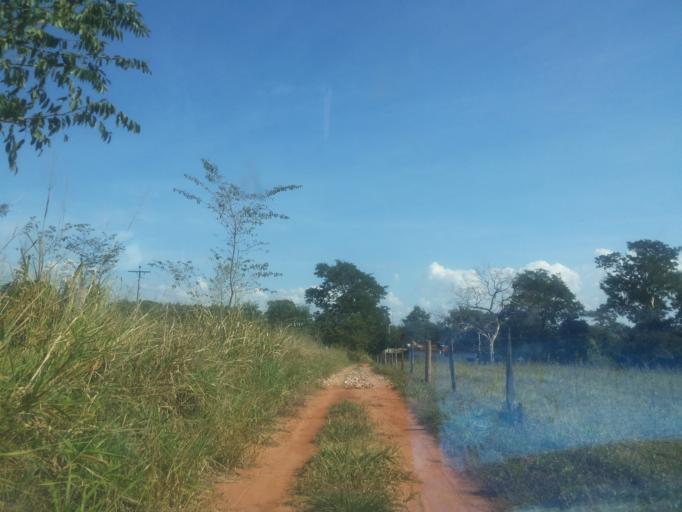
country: BR
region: Minas Gerais
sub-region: Santa Vitoria
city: Santa Vitoria
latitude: -18.9954
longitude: -50.3766
